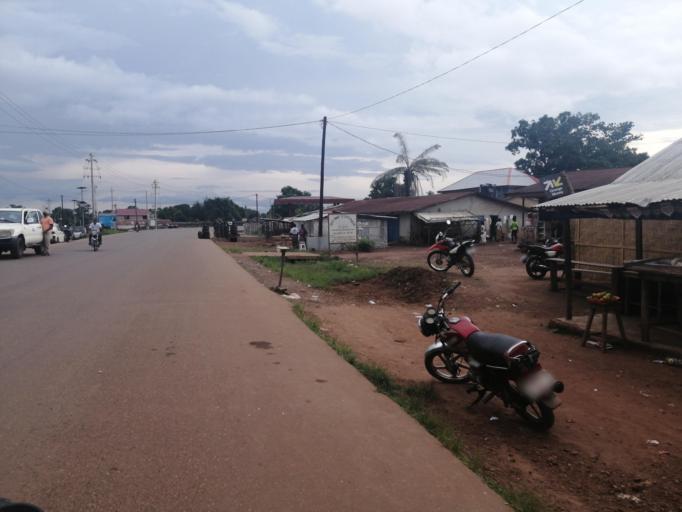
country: SL
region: Northern Province
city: Port Loko
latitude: 8.7752
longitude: -12.7865
